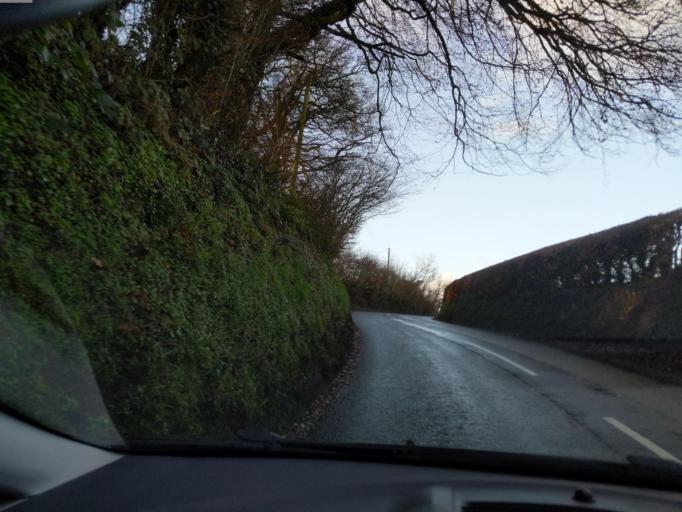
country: GB
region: England
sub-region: Devon
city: Okehampton
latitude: 50.7444
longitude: -4.0152
